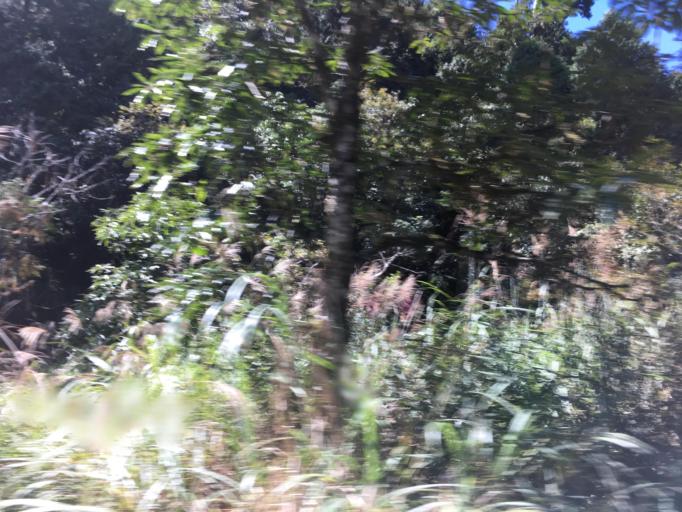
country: TW
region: Taiwan
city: Daxi
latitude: 24.5760
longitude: 121.4136
